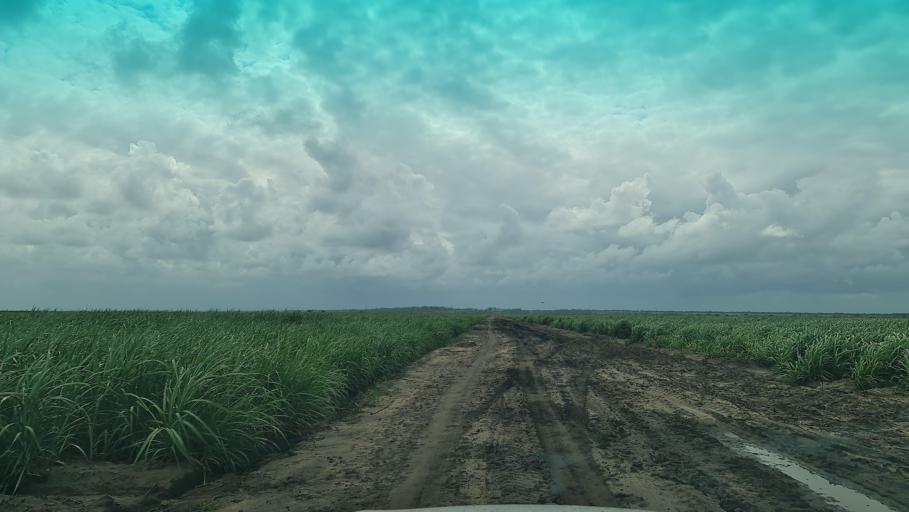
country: MZ
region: Maputo
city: Manhica
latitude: -25.4534
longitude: 32.8315
